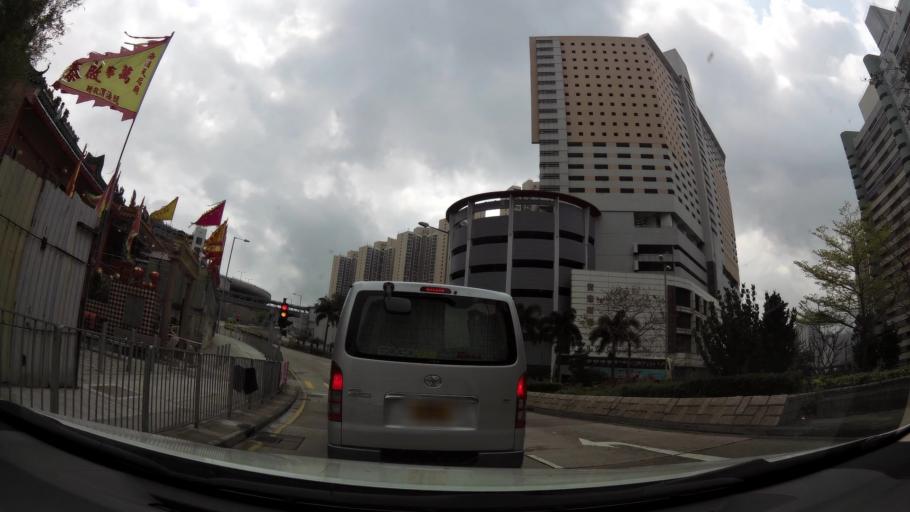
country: HK
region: Kowloon City
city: Kowloon
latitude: 22.3185
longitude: 114.2353
